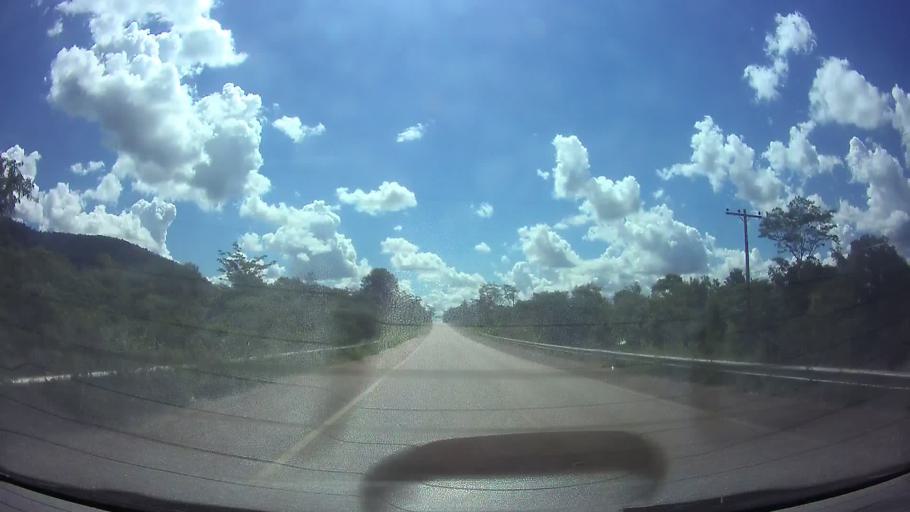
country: PY
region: Paraguari
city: La Colmena
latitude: -25.9163
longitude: -56.7398
